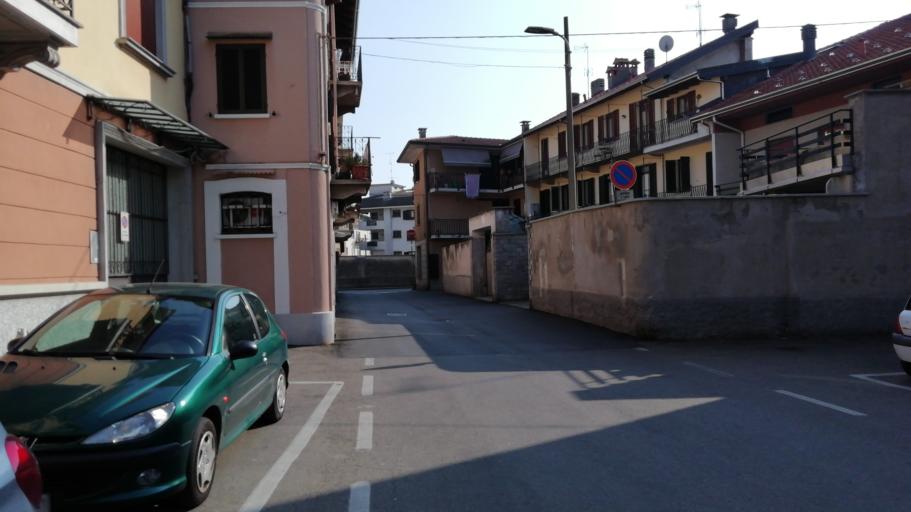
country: IT
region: Piedmont
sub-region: Provincia di Novara
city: Borgomanero
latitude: 45.6965
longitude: 8.4631
